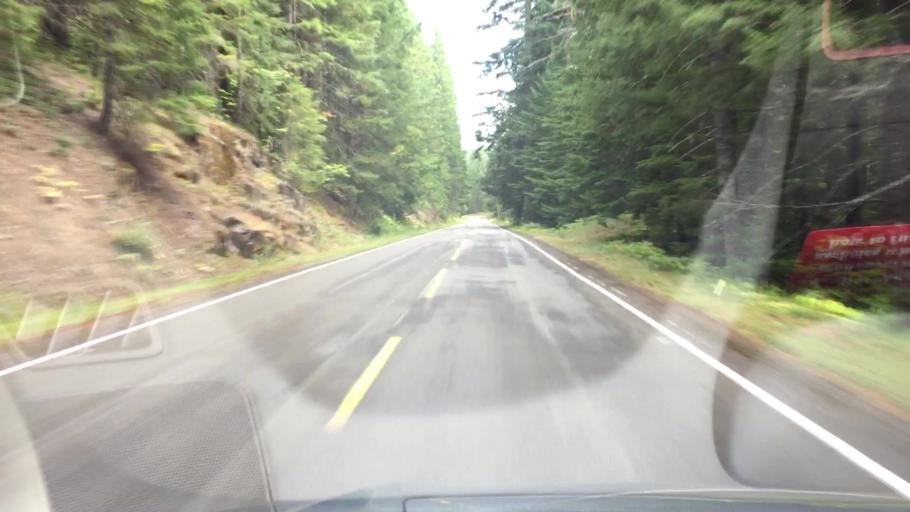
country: US
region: Washington
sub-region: Pierce County
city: Buckley
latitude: 46.7583
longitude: -121.6264
